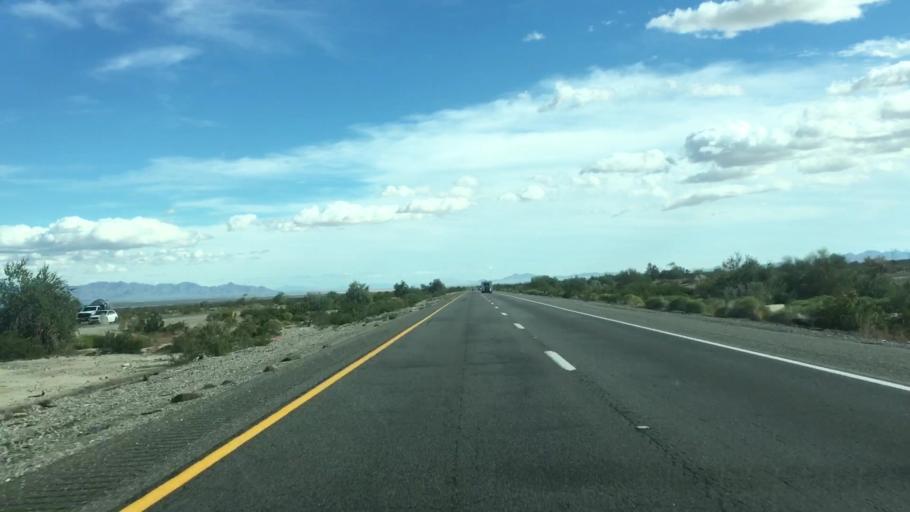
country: US
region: California
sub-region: Riverside County
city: Mesa Verde
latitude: 33.6753
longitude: -115.2202
